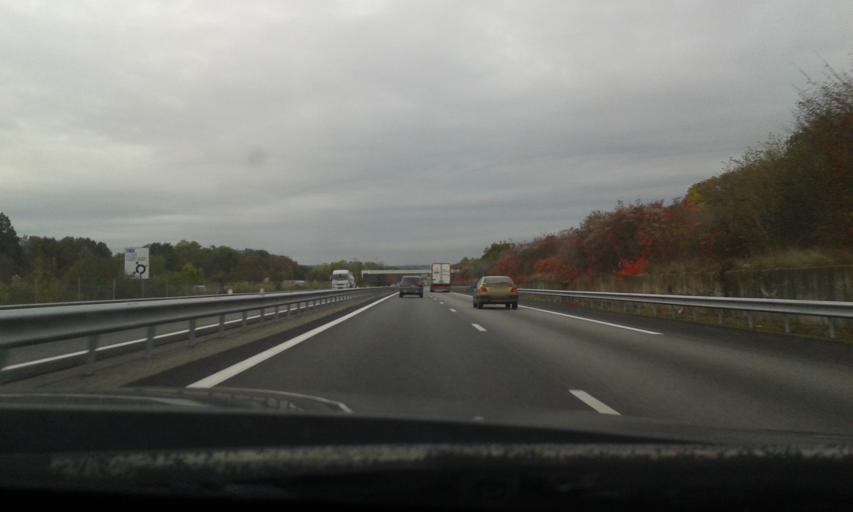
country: FR
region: Haute-Normandie
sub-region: Departement de l'Eure
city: Louviers
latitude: 49.2167
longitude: 1.1805
